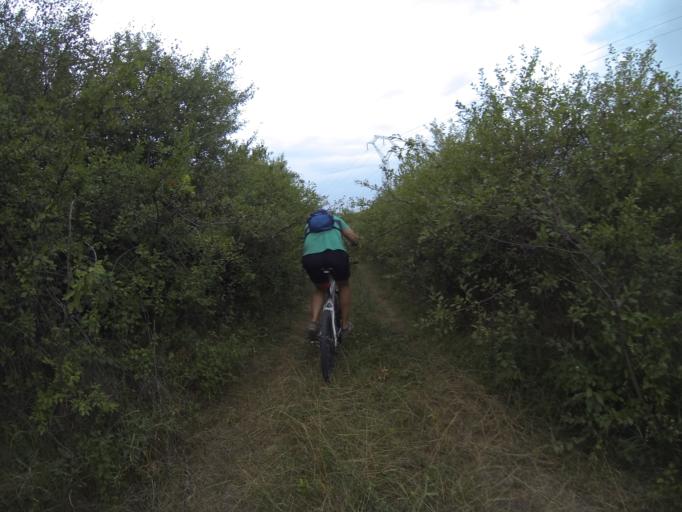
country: RO
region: Dolj
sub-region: Comuna Cotofenii din Fata
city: Cotofenii din Fata
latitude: 44.4811
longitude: 23.6871
